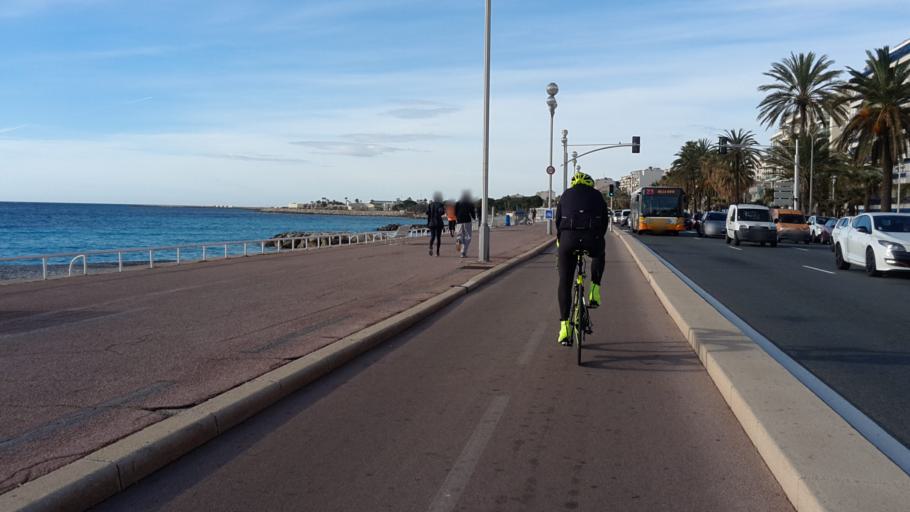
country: FR
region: Provence-Alpes-Cote d'Azur
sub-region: Departement des Alpes-Maritimes
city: Nice
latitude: 43.6834
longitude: 7.2345
